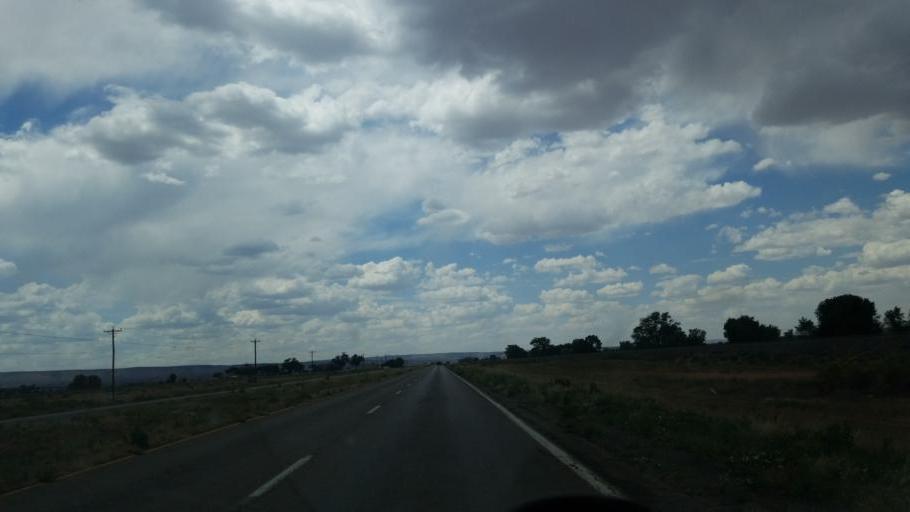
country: US
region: New Mexico
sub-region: Cibola County
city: Milan
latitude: 35.2332
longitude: -107.9330
